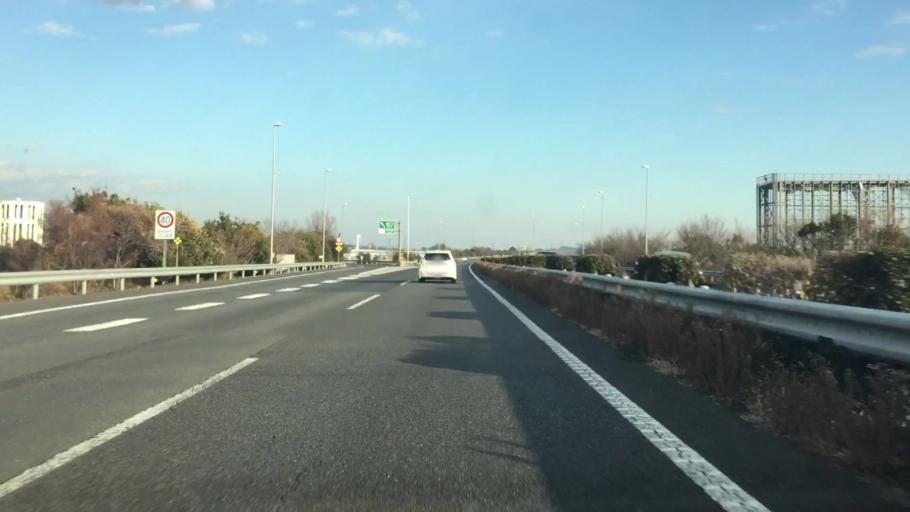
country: JP
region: Gunma
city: Isesaki
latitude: 36.3553
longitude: 139.2164
